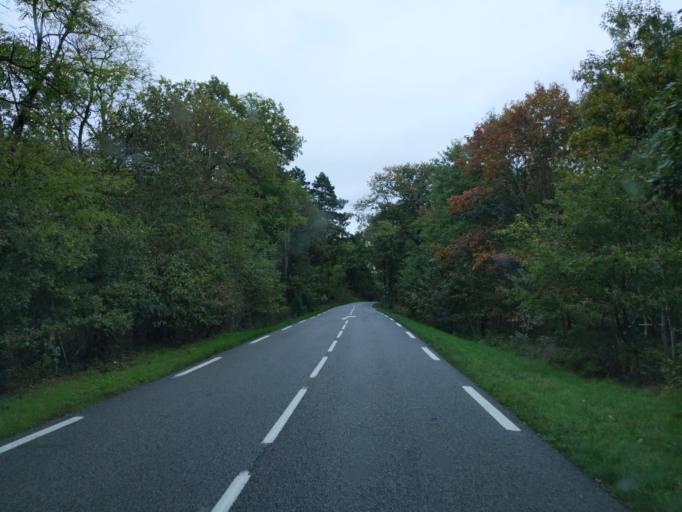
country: FR
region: Ile-de-France
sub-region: Departement des Yvelines
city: Saint-Arnoult-en-Yvelines
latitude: 48.5890
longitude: 1.9336
